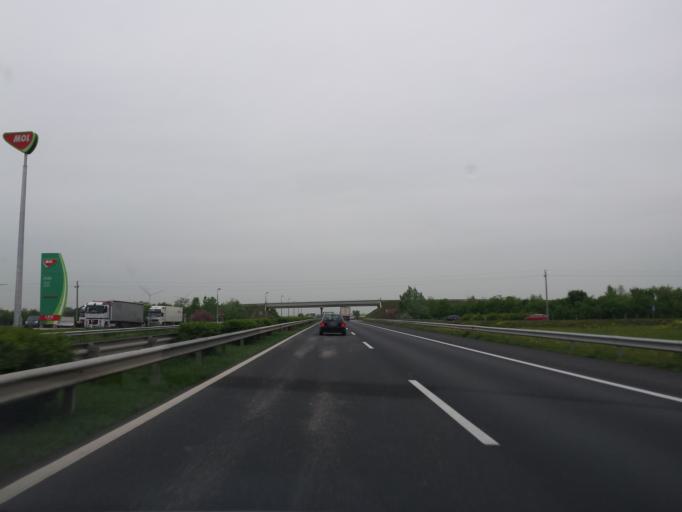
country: HU
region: Gyor-Moson-Sopron
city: Mosonmagyarovar
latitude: 47.8718
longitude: 17.2157
